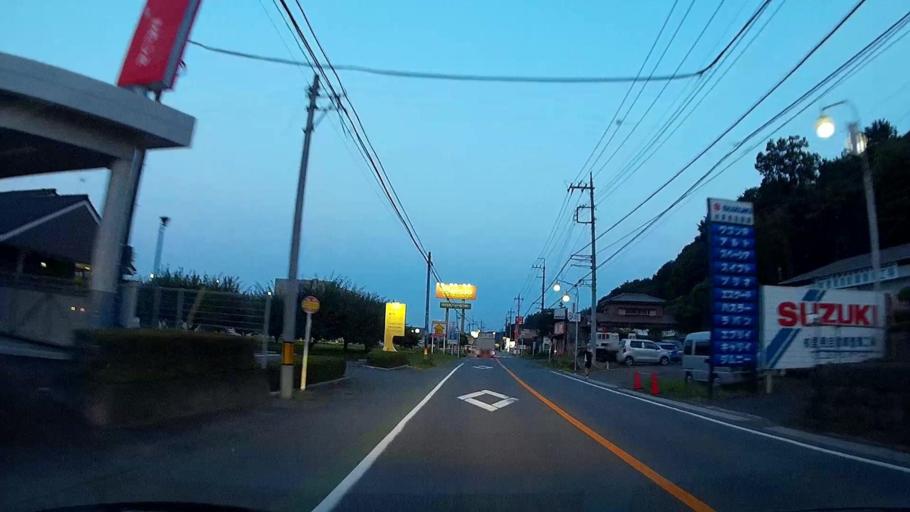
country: JP
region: Gunma
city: Annaka
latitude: 36.3653
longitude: 138.9117
